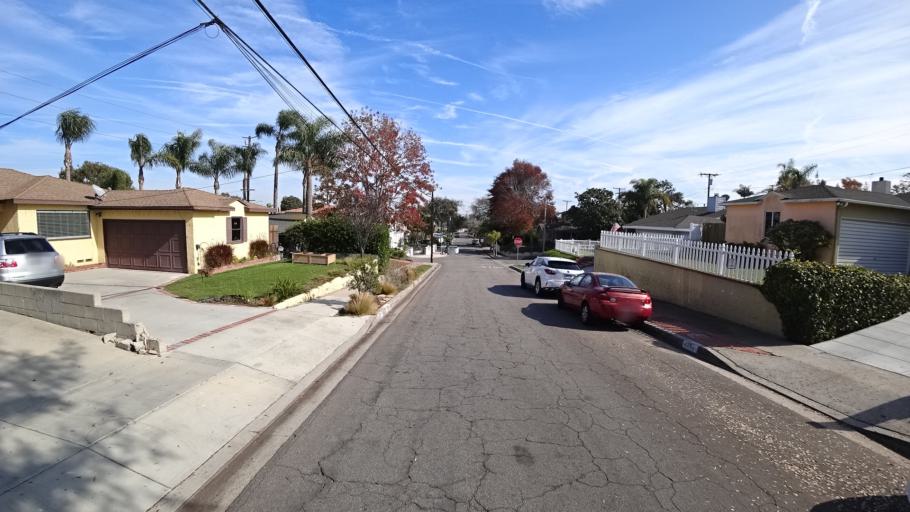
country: US
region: California
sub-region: Los Angeles County
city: Manhattan Beach
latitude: 33.8942
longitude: -118.3939
